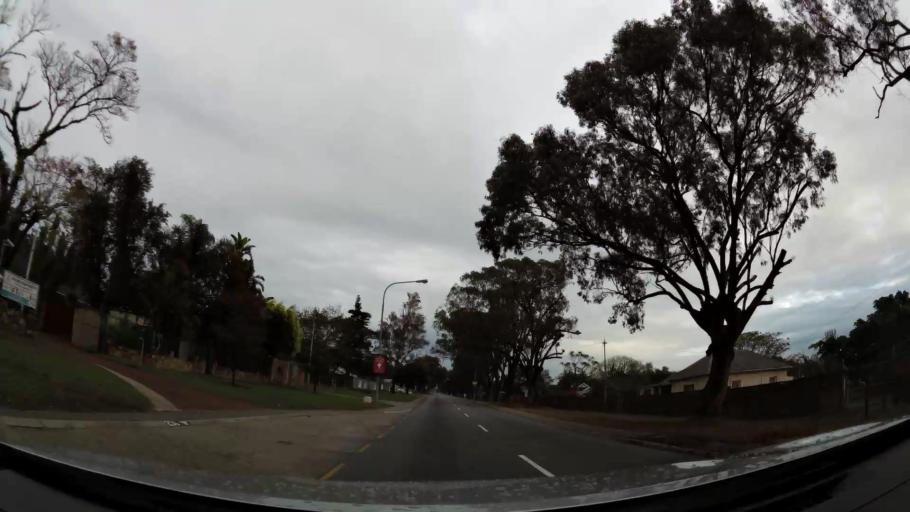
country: ZA
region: Eastern Cape
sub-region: Nelson Mandela Bay Metropolitan Municipality
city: Port Elizabeth
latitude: -33.9823
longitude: 25.5701
